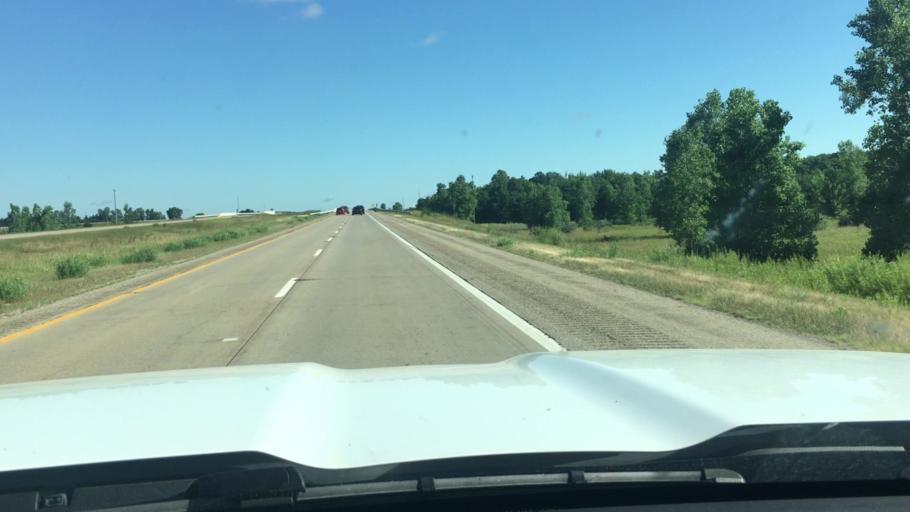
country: US
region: Michigan
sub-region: Clinton County
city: Saint Johns
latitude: 42.9985
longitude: -84.5186
